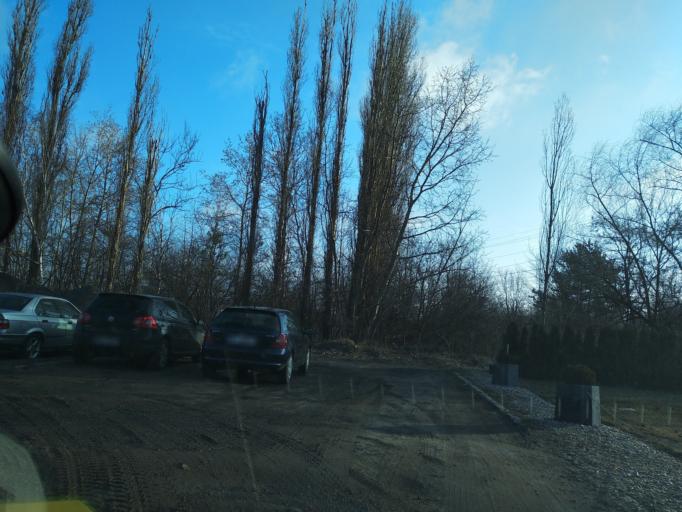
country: PL
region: Masovian Voivodeship
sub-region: Powiat piaseczynski
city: Piaseczno
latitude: 52.0899
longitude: 21.0327
